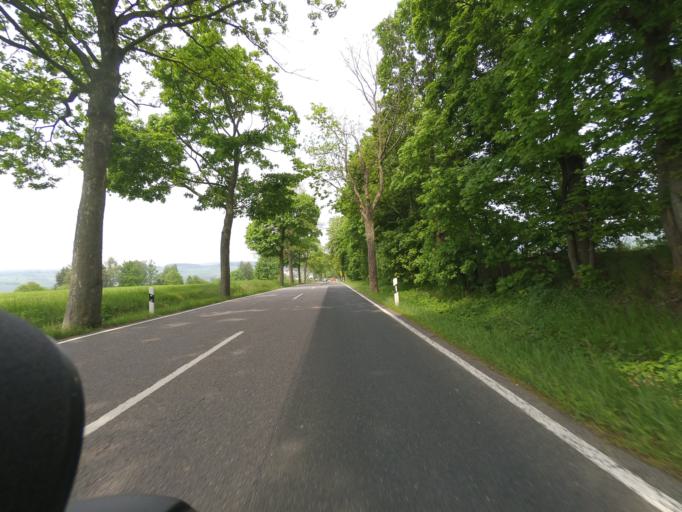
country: DE
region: Saxony
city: Wolkenstein
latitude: 50.6505
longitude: 13.0837
